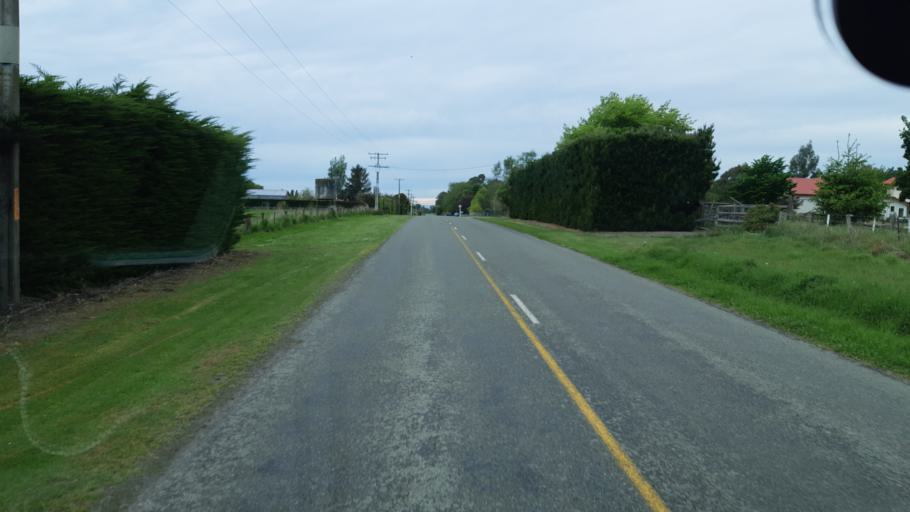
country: NZ
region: Canterbury
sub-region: Timaru District
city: Timaru
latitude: -44.4115
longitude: 171.1862
